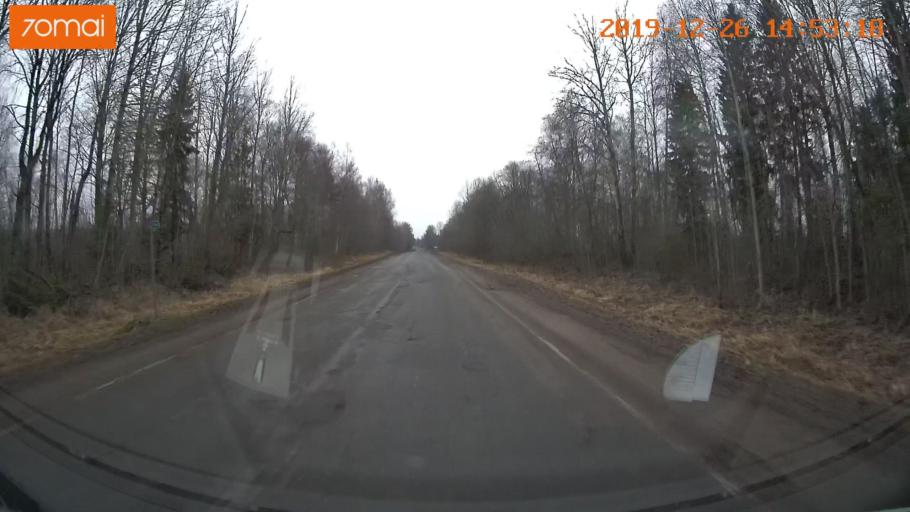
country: RU
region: Jaroslavl
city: Rybinsk
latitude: 58.3163
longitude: 38.8903
